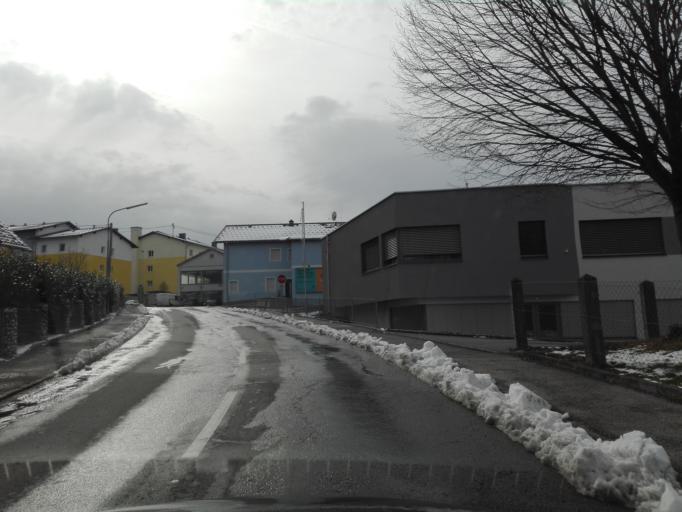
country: AT
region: Upper Austria
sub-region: Politischer Bezirk Rohrbach
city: Atzesberg
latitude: 48.4970
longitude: 13.8936
